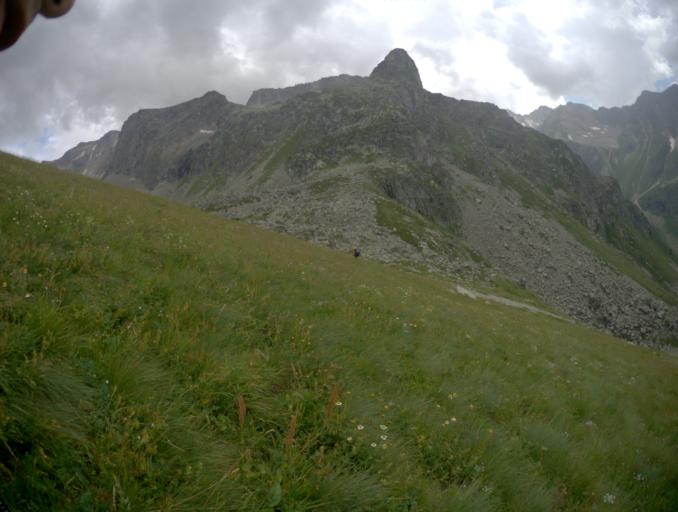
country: RU
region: Karachayevo-Cherkesiya
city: Uchkulan
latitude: 43.2916
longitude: 42.0792
